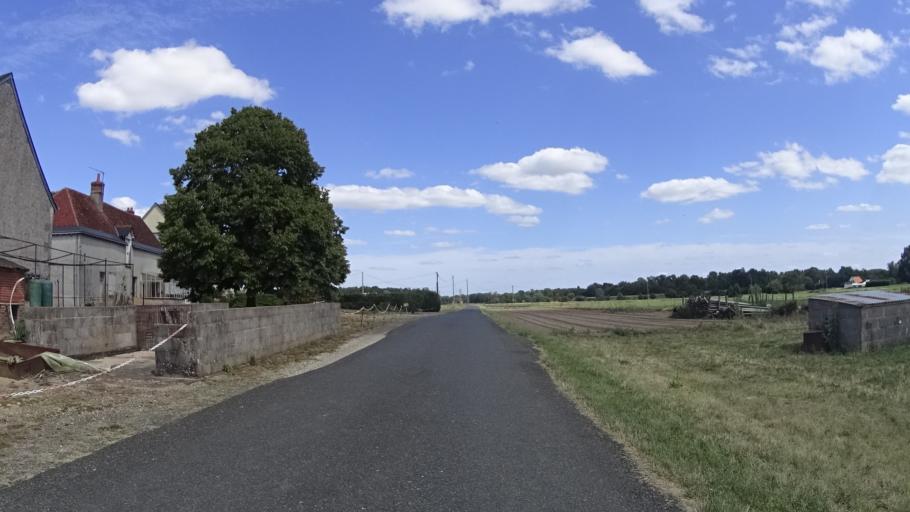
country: FR
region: Centre
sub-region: Departement d'Indre-et-Loire
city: Vernou-sur-Brenne
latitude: 47.4032
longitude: 0.8520
